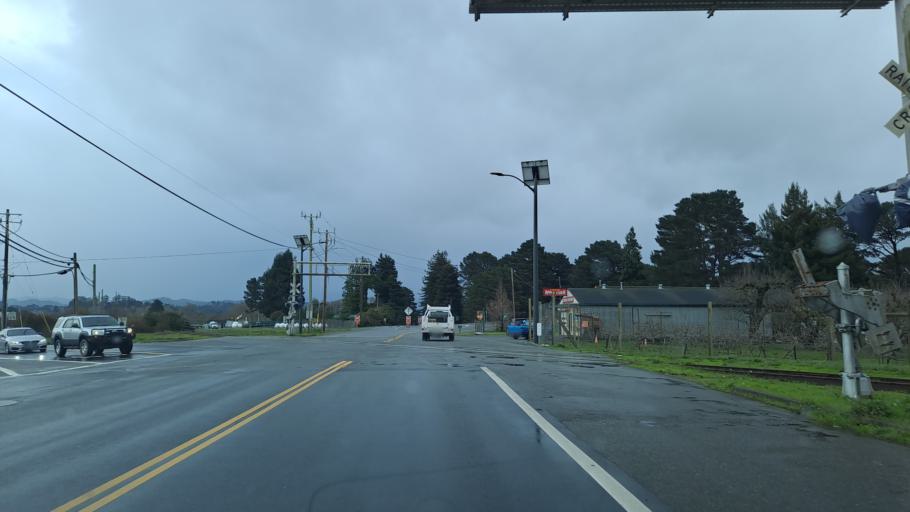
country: US
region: California
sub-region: Humboldt County
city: Fortuna
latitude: 40.5901
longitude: -124.1546
